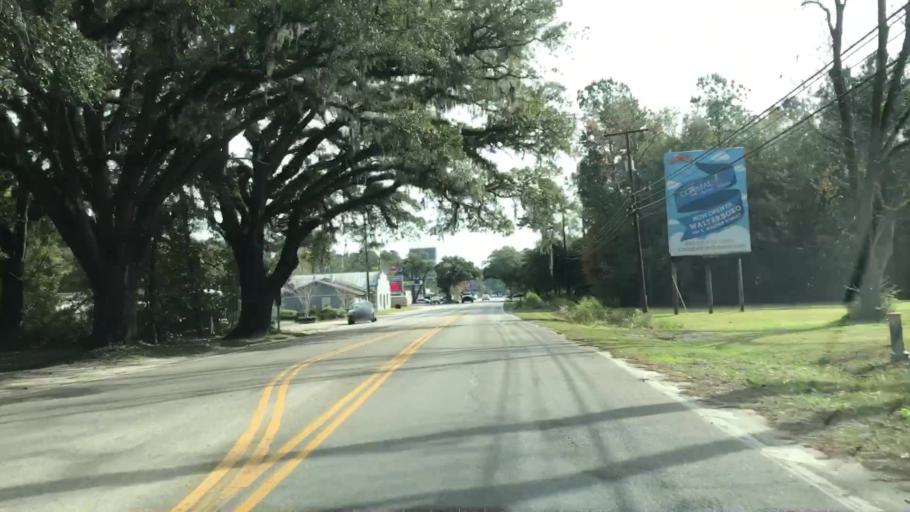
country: US
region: South Carolina
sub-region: Colleton County
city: Walterboro
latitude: 32.8967
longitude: -80.6442
